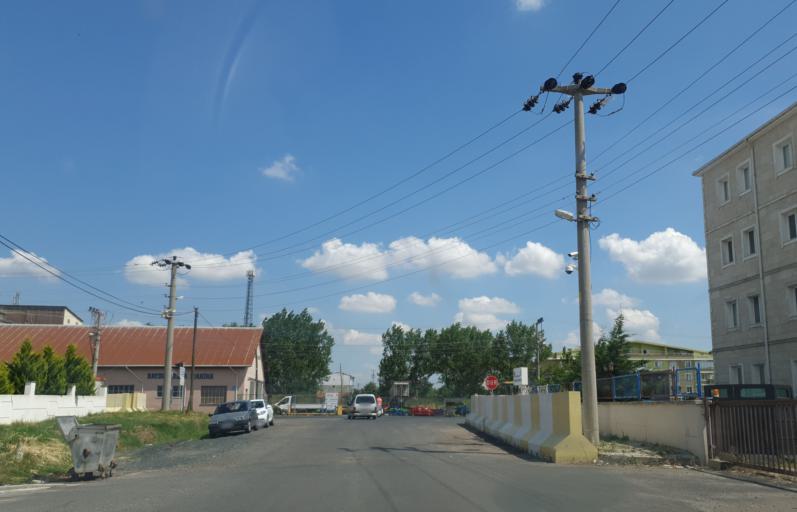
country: TR
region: Tekirdag
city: Muratli
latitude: 41.1787
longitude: 27.5026
